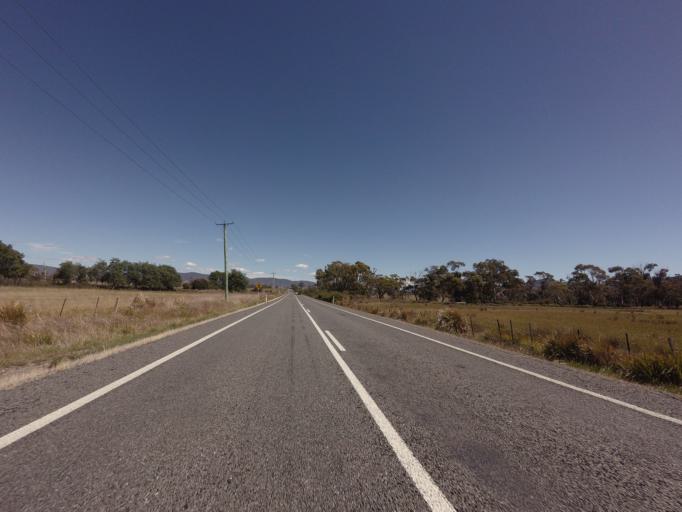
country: AU
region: Tasmania
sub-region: Northern Midlands
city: Evandale
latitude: -41.7668
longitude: 147.7436
